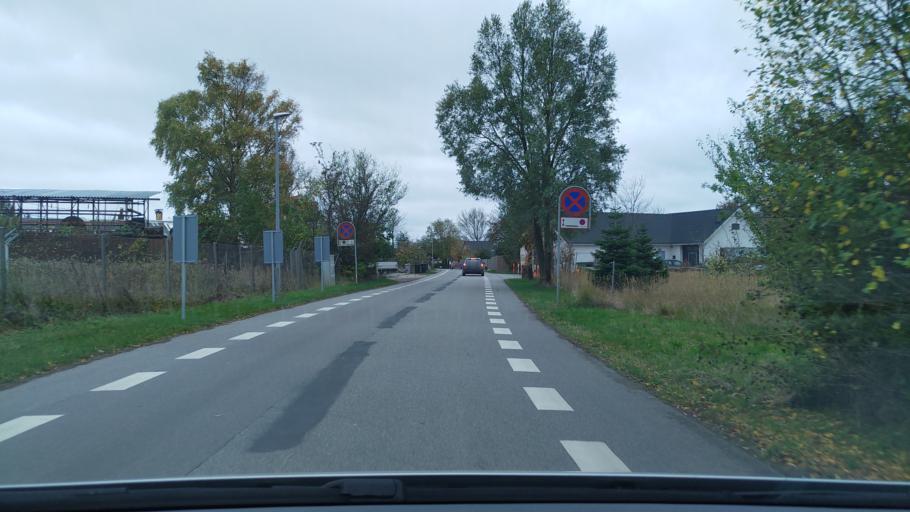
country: DK
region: Capital Region
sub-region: Tarnby Kommune
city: Tarnby
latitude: 55.5938
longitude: 12.5975
